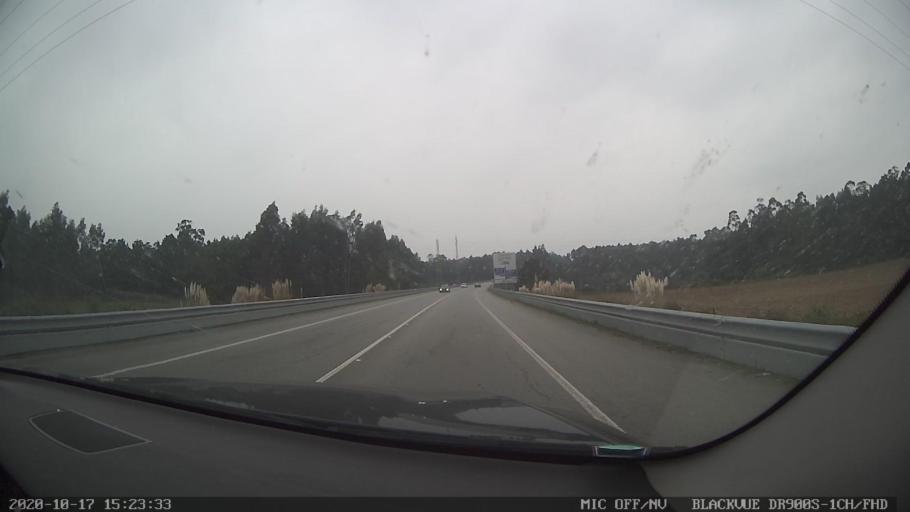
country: PT
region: Braga
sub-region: Esposende
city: Esposende
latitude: 41.5287
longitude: -8.7410
